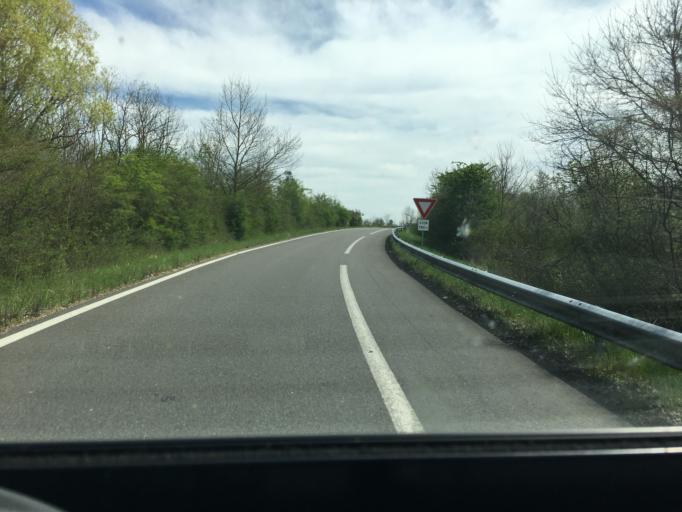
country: FR
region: Lorraine
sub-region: Departement de Meurthe-et-Moselle
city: Ecrouves
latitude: 48.6491
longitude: 5.8673
